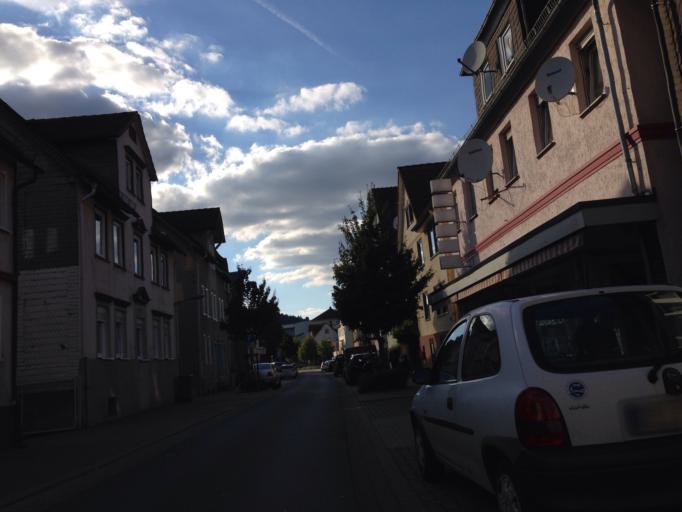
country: DE
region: Hesse
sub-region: Regierungsbezirk Giessen
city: Biedenkopf
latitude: 50.9117
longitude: 8.5291
